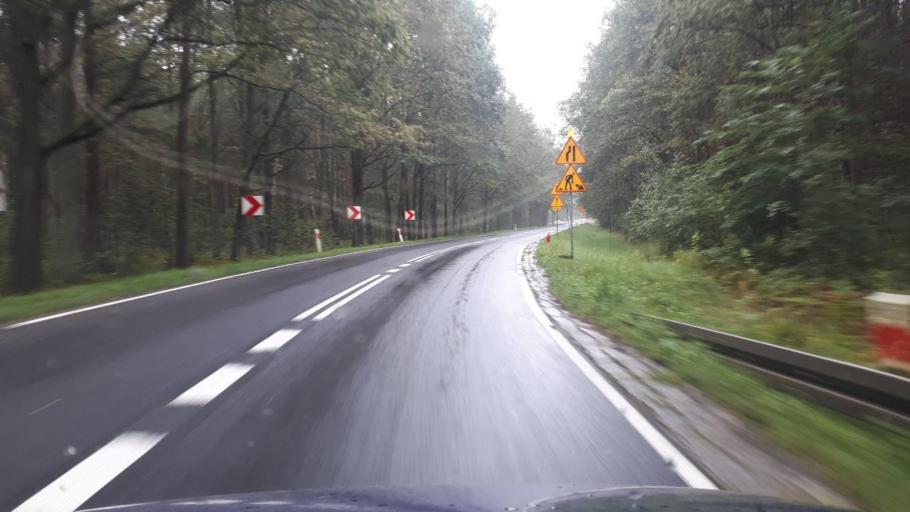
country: PL
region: Silesian Voivodeship
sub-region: Powiat lubliniecki
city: Sierakow Slaski
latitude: 50.8115
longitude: 18.5551
